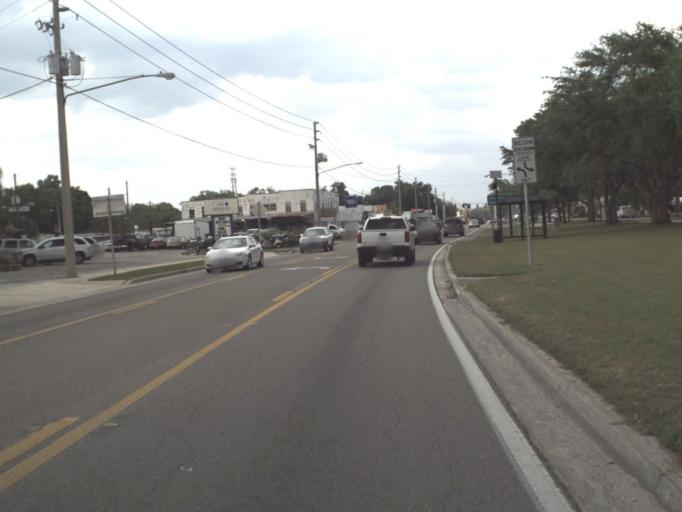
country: US
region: Florida
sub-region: Lake County
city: Umatilla
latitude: 28.9317
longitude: -81.6669
